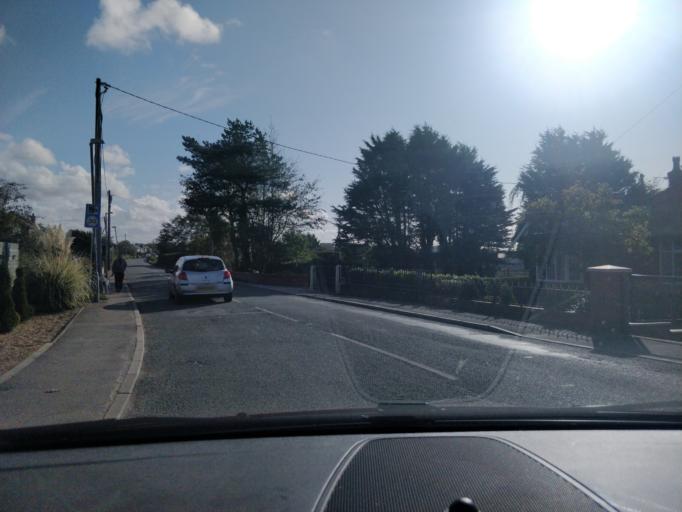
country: GB
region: England
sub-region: Lancashire
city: Banks
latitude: 53.6899
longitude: -2.9149
